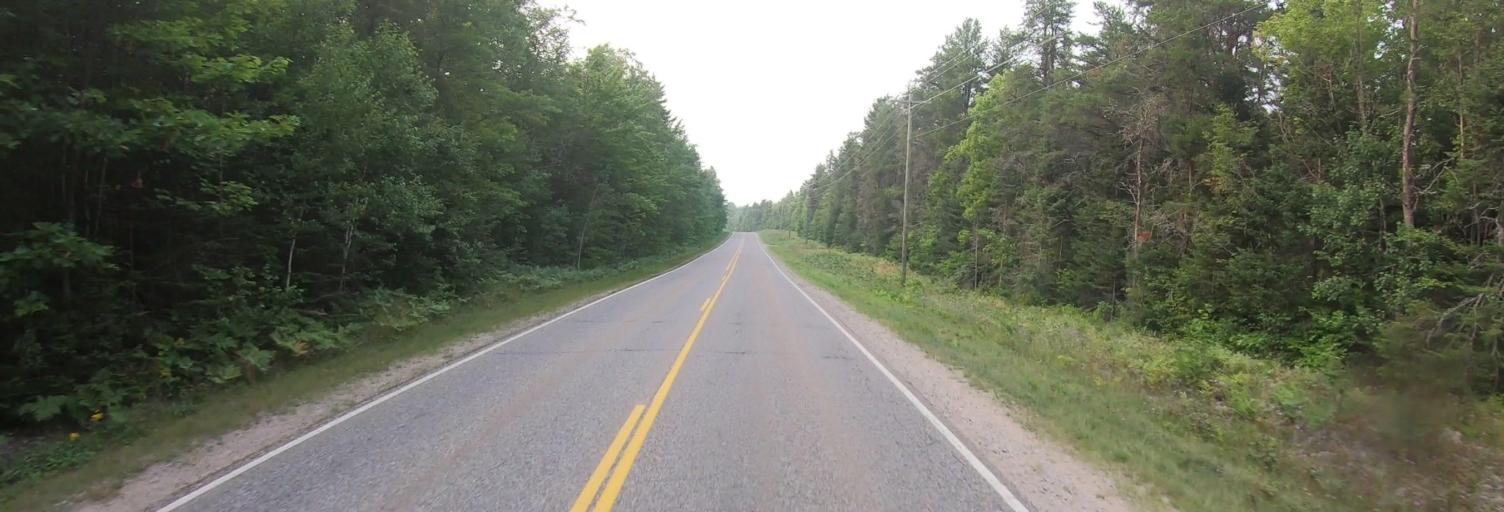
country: US
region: Michigan
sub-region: Chippewa County
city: Sault Ste. Marie
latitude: 46.4744
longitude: -84.6227
